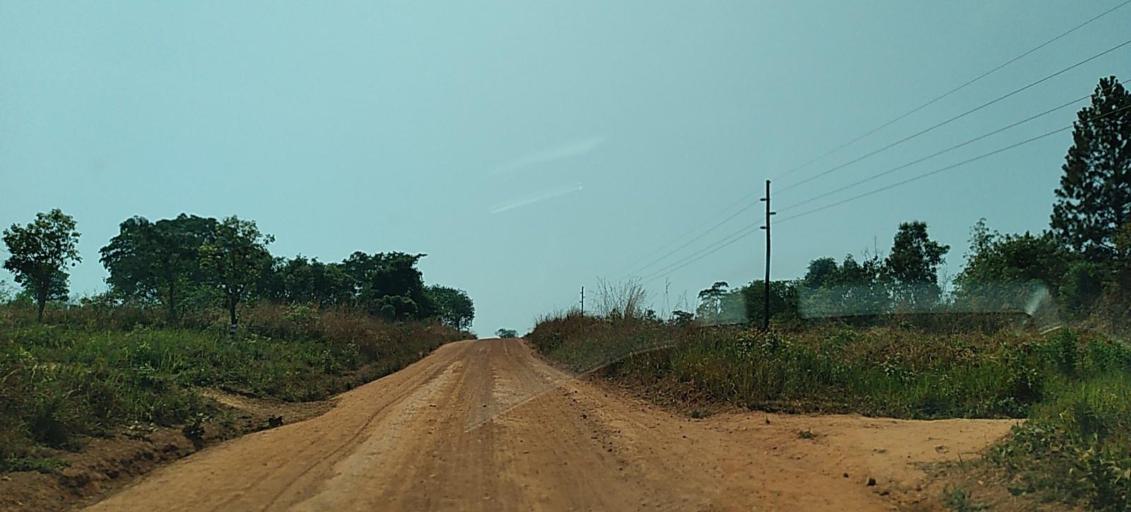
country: ZM
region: North-Western
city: Kansanshi
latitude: -12.0068
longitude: 26.5751
